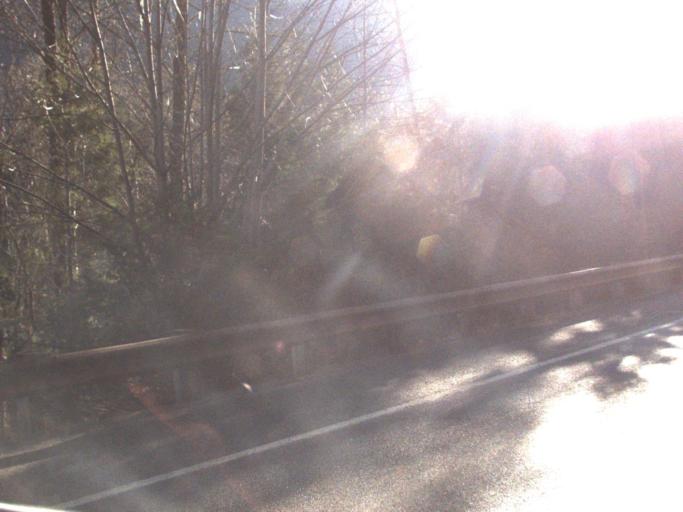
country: US
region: Washington
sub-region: Snohomish County
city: Darrington
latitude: 48.5756
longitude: -121.4075
